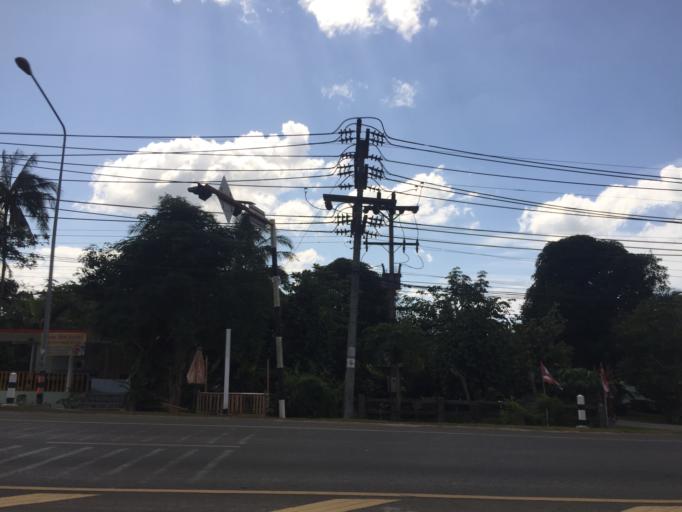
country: TH
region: Phangnga
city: Ban Ao Nang
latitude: 8.0730
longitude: 98.8393
